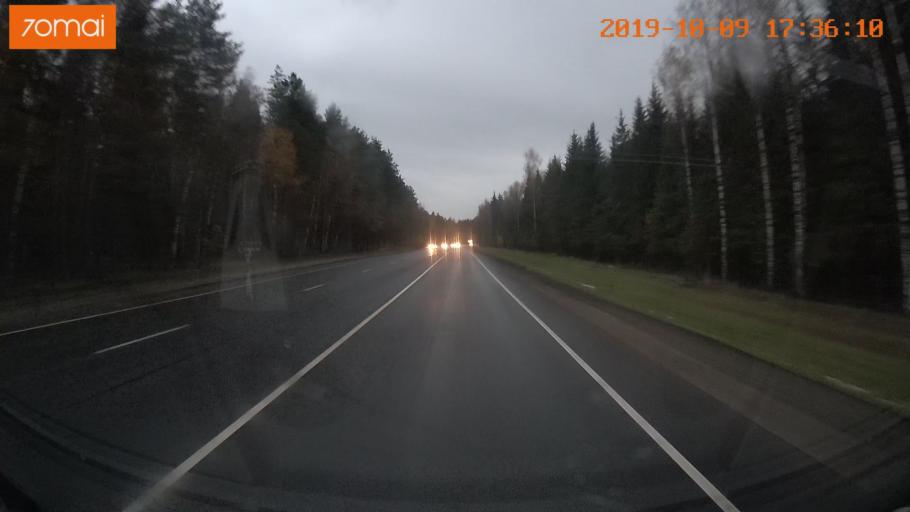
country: RU
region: Ivanovo
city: Bogorodskoye
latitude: 57.0825
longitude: 40.9982
